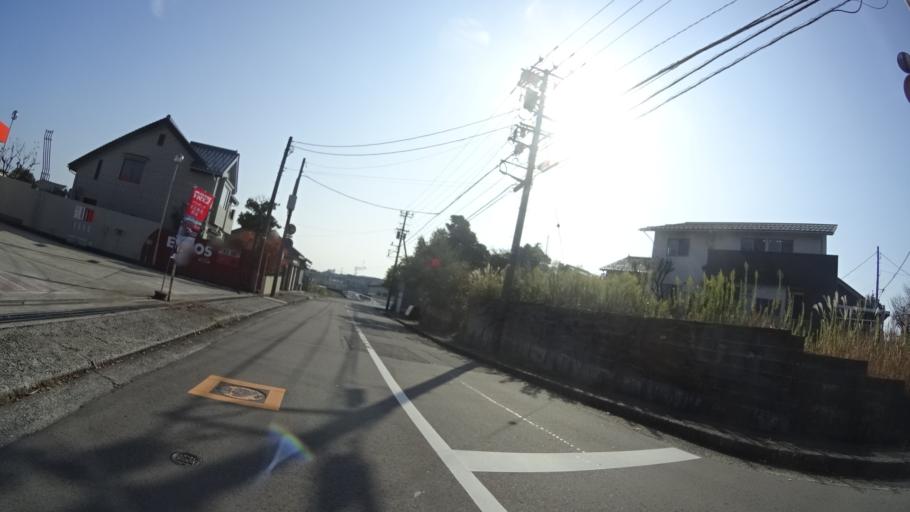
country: JP
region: Toyama
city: Nishishinminato
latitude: 36.7957
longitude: 137.0506
